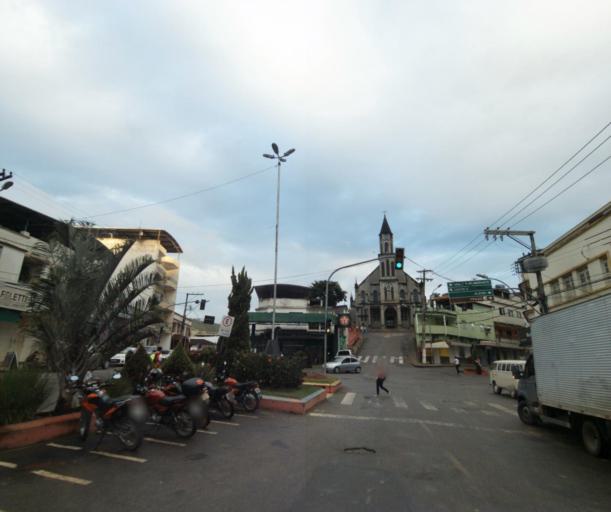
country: BR
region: Espirito Santo
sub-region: Muniz Freire
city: Muniz Freire
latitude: -20.4640
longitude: -41.4135
